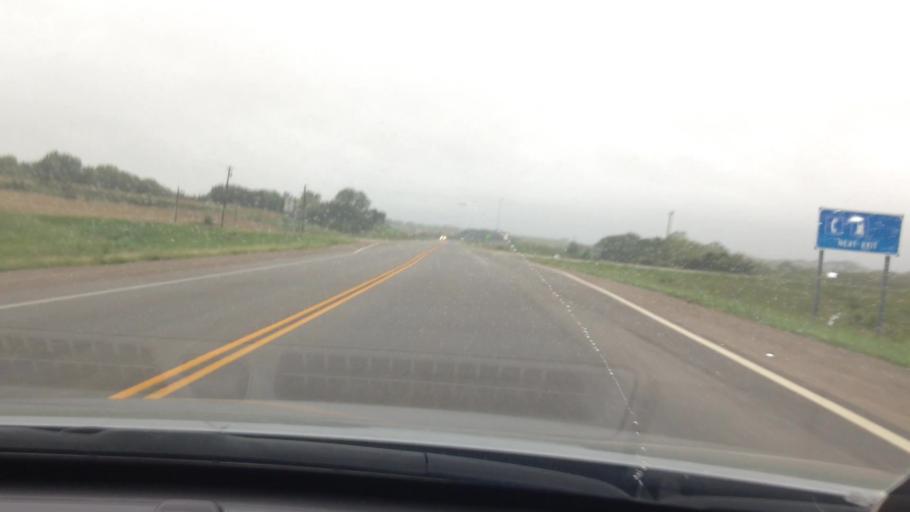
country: US
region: Kansas
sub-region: Doniphan County
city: Troy
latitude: 39.7944
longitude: -95.0859
